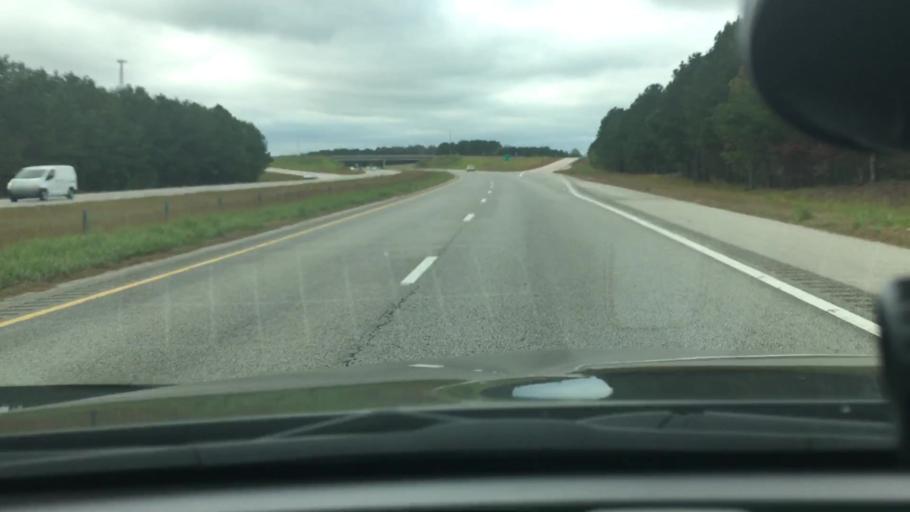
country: US
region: North Carolina
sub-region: Wilson County
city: Wilson
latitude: 35.6732
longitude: -77.7998
